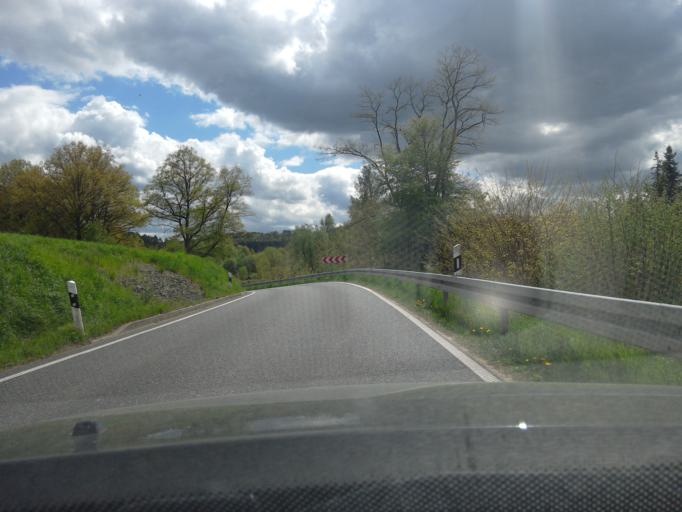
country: DE
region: Bavaria
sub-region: Regierungsbezirk Unterfranken
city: Aura im Sinngrund
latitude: 50.2123
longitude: 9.4888
